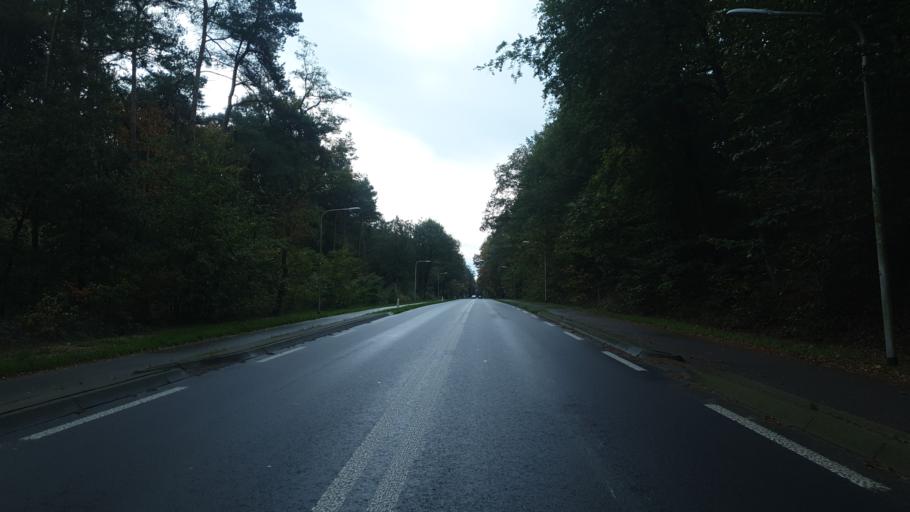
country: NL
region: Gelderland
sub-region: Gemeente Groesbeek
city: Berg en Dal
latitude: 51.8076
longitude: 5.8927
